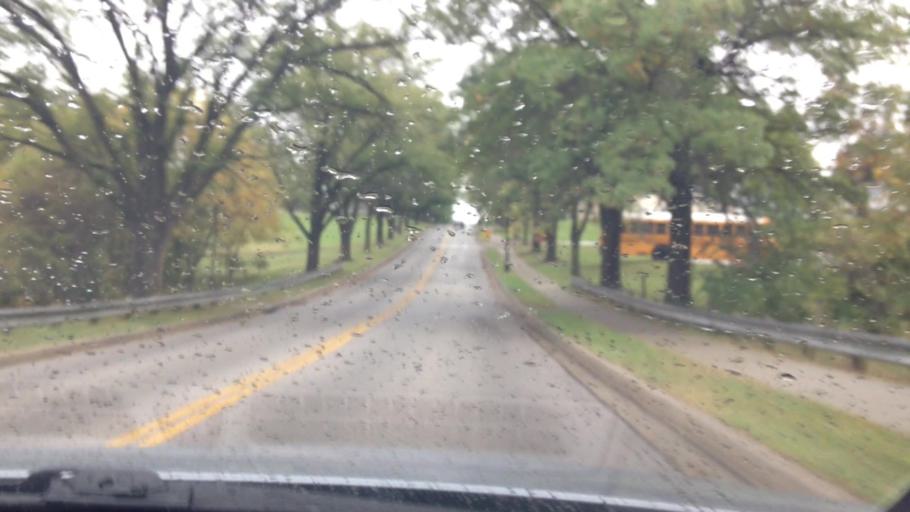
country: US
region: Kansas
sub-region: Leavenworth County
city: Leavenworth
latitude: 39.3426
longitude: -94.9319
